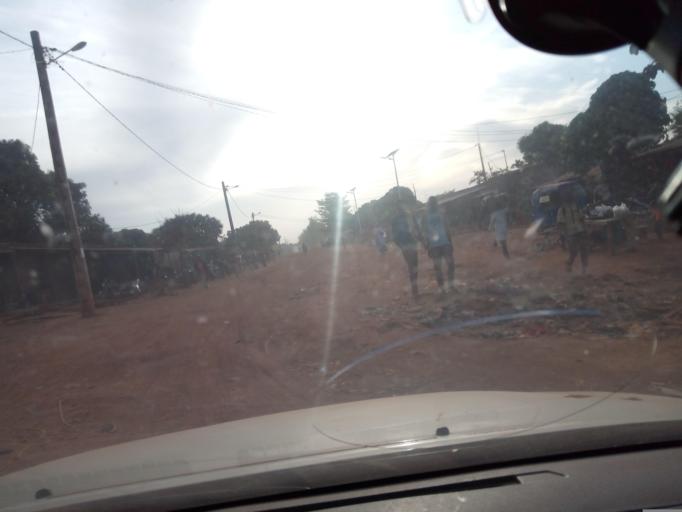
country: ML
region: Sikasso
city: Sikasso
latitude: 11.3114
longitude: -5.6531
